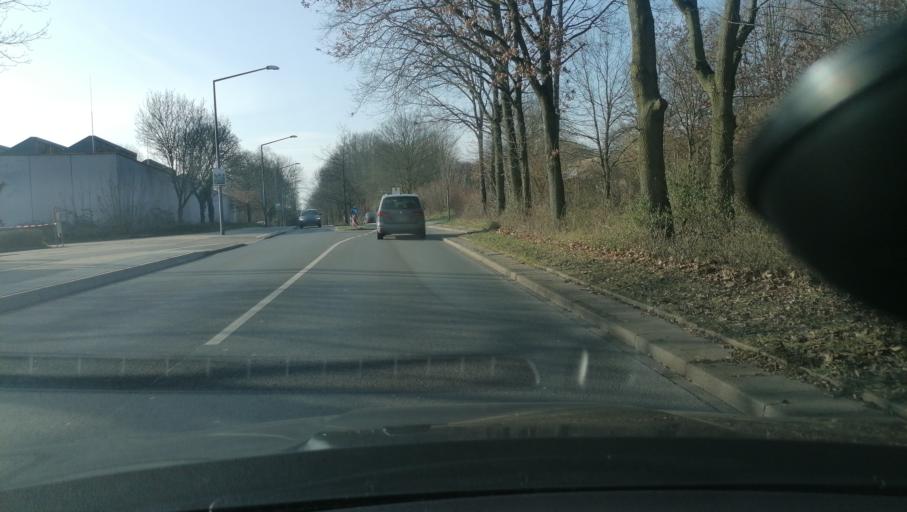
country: DE
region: North Rhine-Westphalia
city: Herten
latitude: 51.6094
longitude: 7.1387
